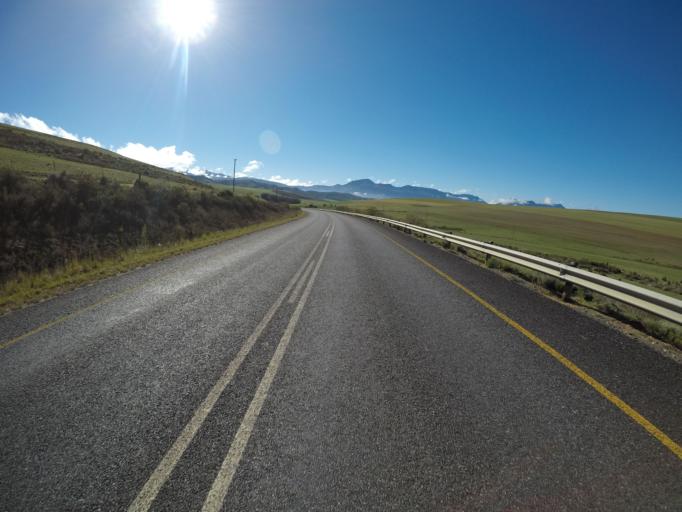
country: ZA
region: Western Cape
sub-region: Overberg District Municipality
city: Caledon
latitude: -34.1311
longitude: 19.5127
